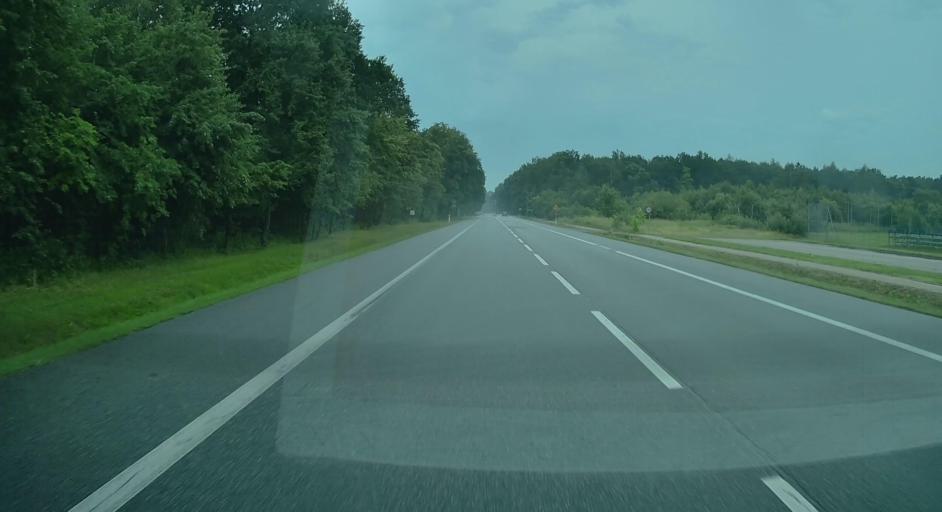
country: PL
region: Masovian Voivodeship
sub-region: Powiat siedlecki
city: Zbuczyn
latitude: 52.0845
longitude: 22.4597
